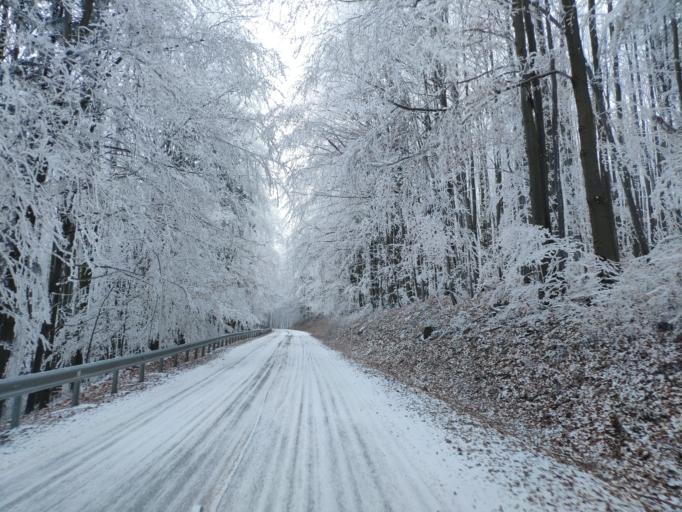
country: SK
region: Kosicky
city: Dobsina
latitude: 48.8072
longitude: 20.4836
